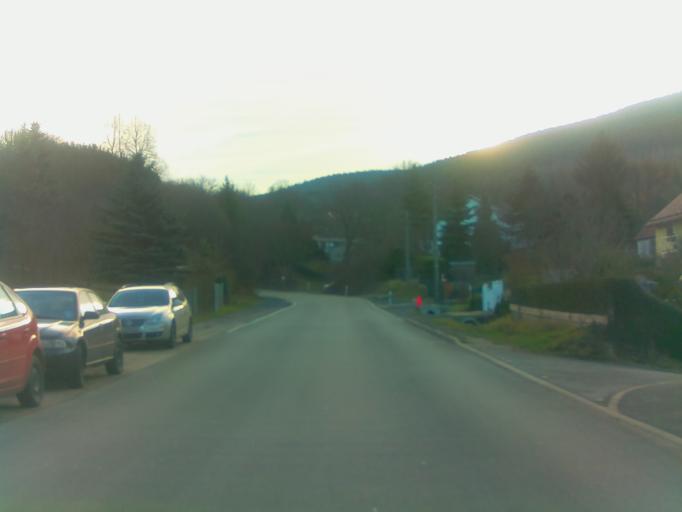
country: DE
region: Thuringia
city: Bad Blankenburg
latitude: 50.6761
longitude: 11.2778
